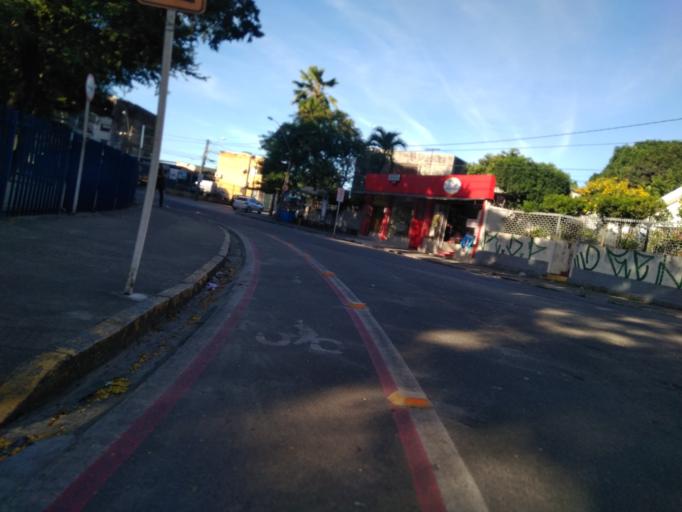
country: BR
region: Pernambuco
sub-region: Recife
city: Recife
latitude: -8.0820
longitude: -34.9383
